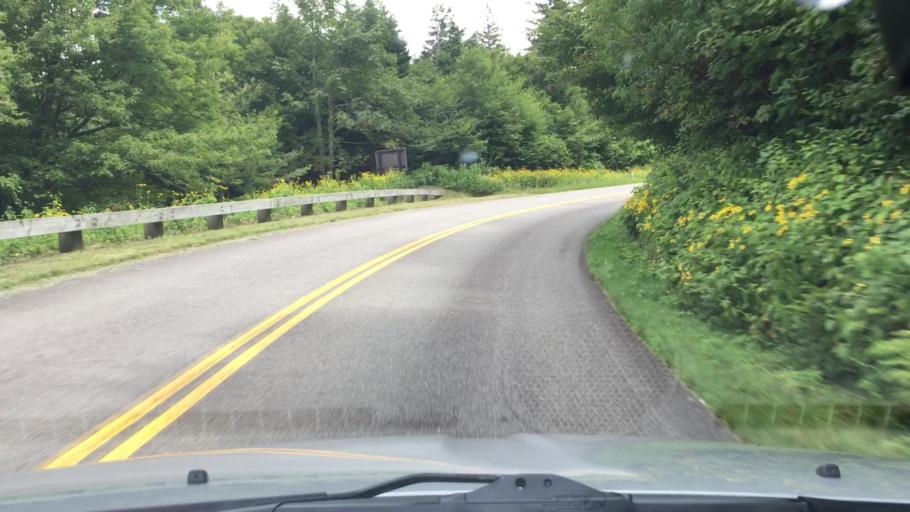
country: US
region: North Carolina
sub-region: Buncombe County
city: Black Mountain
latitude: 35.7157
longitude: -82.2747
